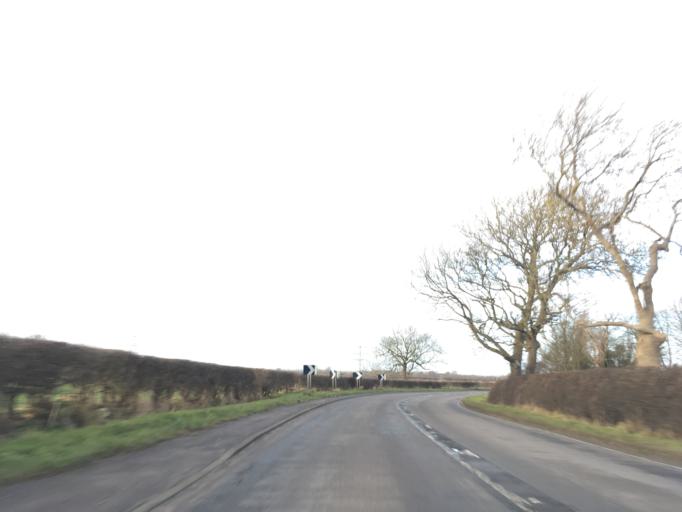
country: GB
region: England
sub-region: Nottinghamshire
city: South Collingham
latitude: 53.1629
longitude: -0.7641
